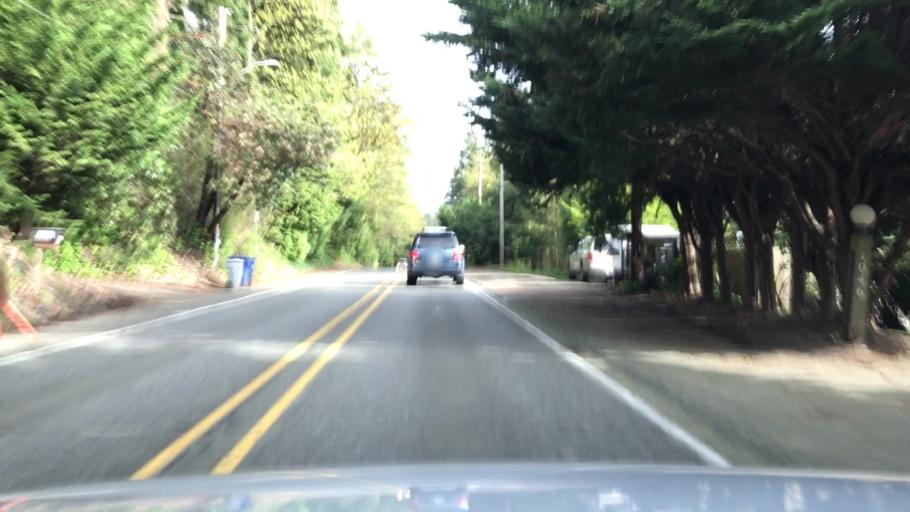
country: US
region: Washington
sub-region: King County
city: West Lake Sammamish
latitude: 47.6001
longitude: -122.1109
